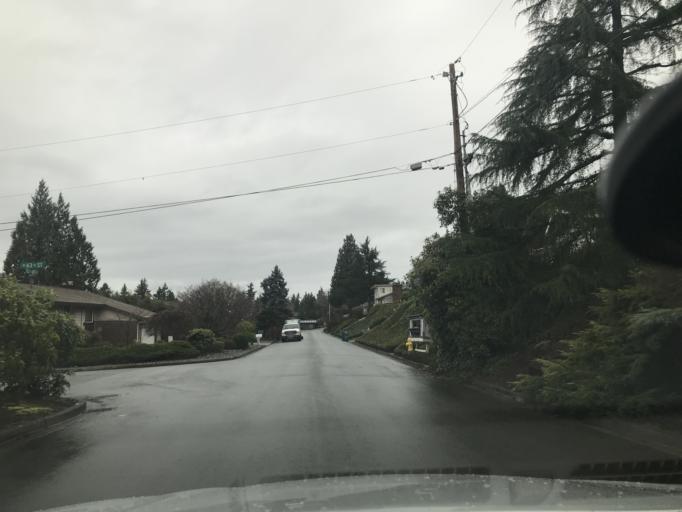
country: US
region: Washington
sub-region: King County
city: Kirkland
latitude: 47.6629
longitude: -122.1891
